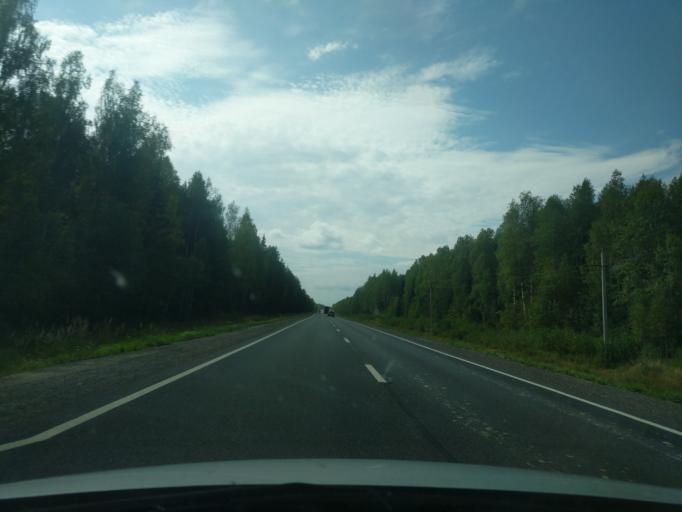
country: RU
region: Kostroma
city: Kadyy
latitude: 57.8105
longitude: 43.2241
